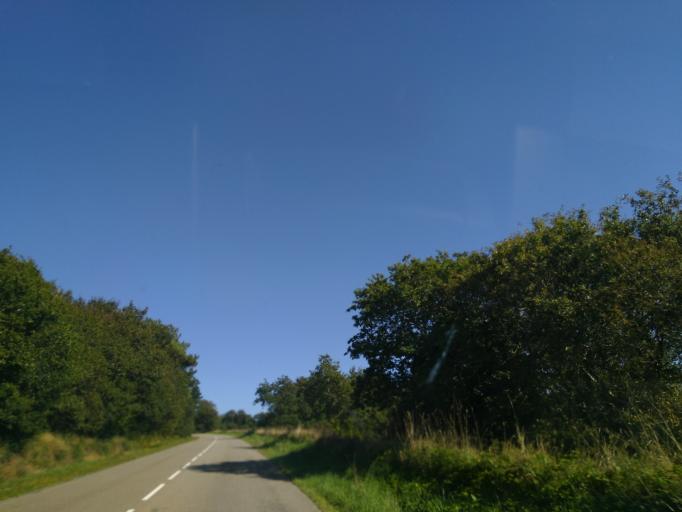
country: FR
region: Brittany
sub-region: Departement du Finistere
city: Hopital-Camfrout
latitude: 48.2711
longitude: -4.2574
